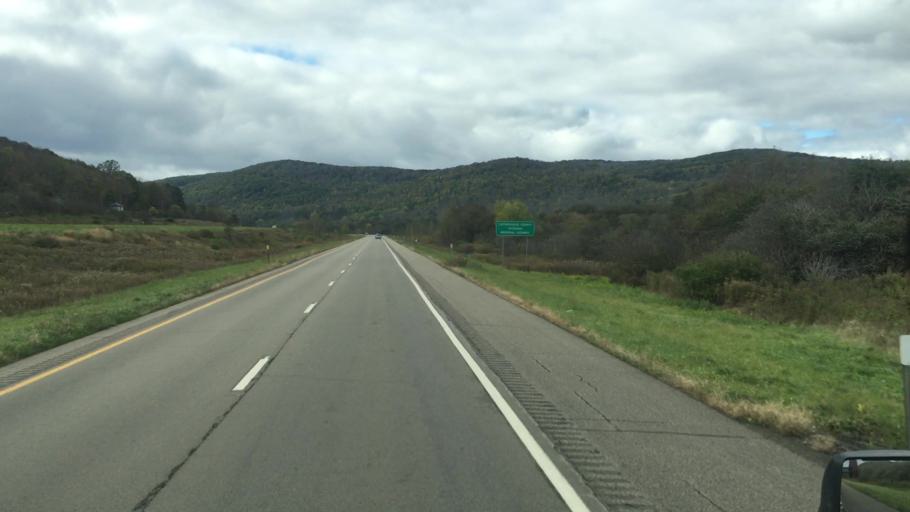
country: US
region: New York
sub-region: Allegany County
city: Cuba
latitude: 42.2154
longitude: -78.3116
